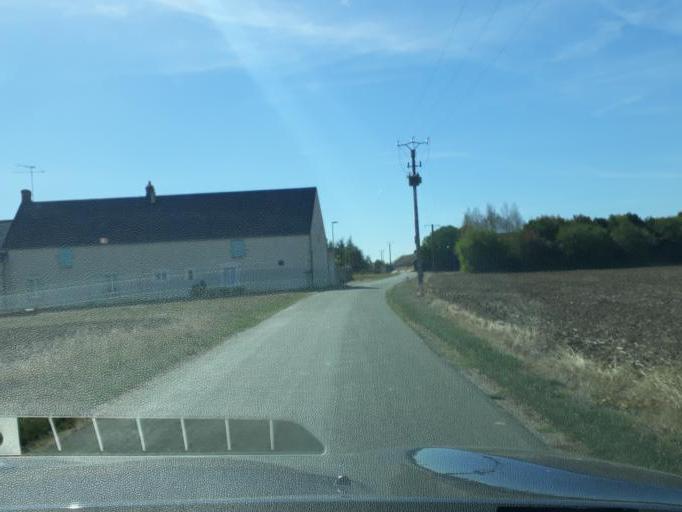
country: FR
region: Centre
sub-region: Departement du Loir-et-Cher
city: Ouzouer-le-Marche
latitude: 47.8732
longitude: 1.5674
